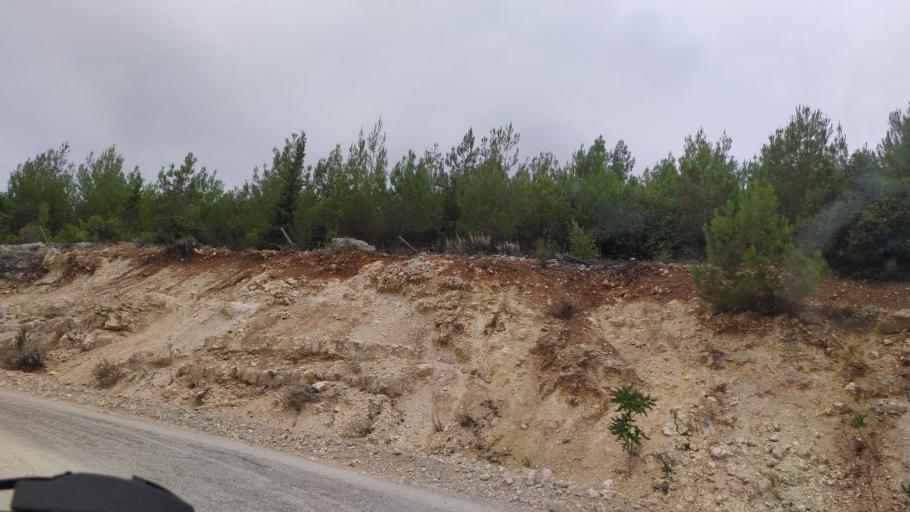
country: TR
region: Mersin
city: Silifke
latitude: 36.5431
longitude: 33.9292
